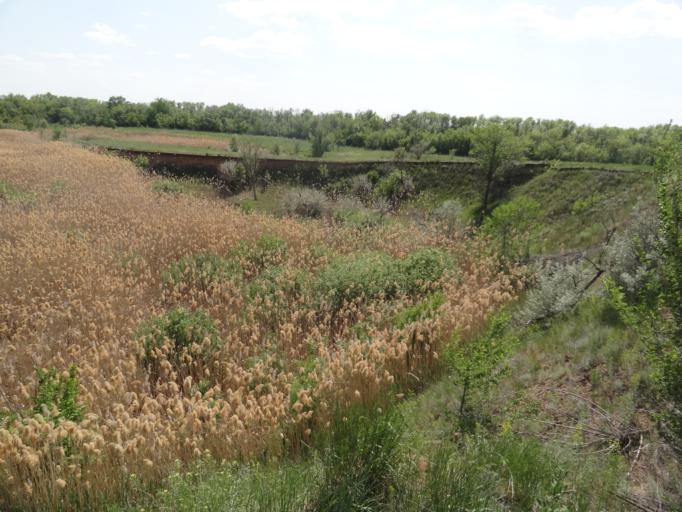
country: RU
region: Saratov
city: Privolzhskiy
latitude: 51.3479
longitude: 46.1437
